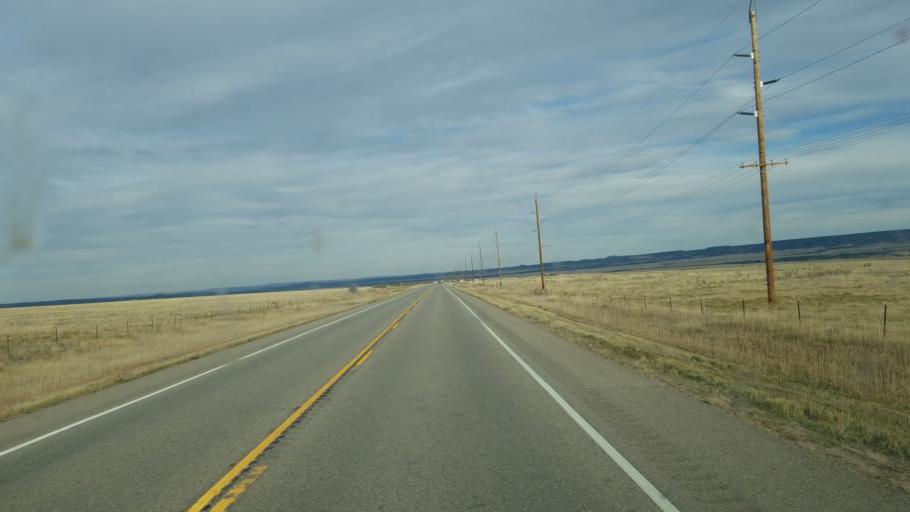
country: US
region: Colorado
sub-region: Huerfano County
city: Walsenburg
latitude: 37.5417
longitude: -105.0551
